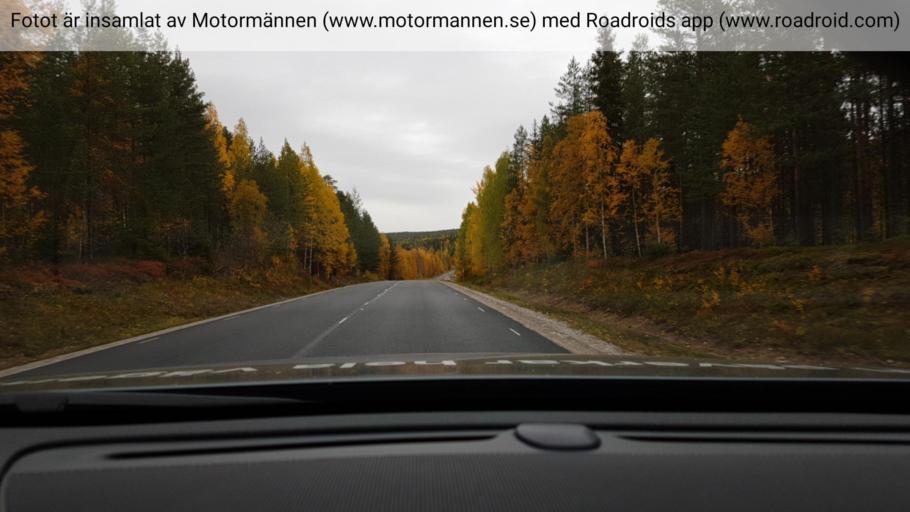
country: SE
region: Norrbotten
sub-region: Overkalix Kommun
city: OEverkalix
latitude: 66.4558
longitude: 22.7896
